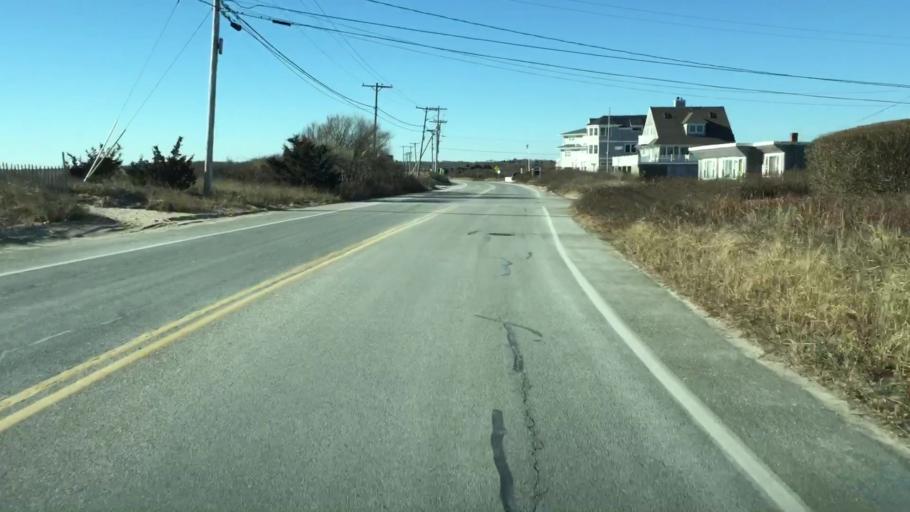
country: US
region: Massachusetts
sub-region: Barnstable County
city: Falmouth
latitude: 41.5419
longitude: -70.6210
